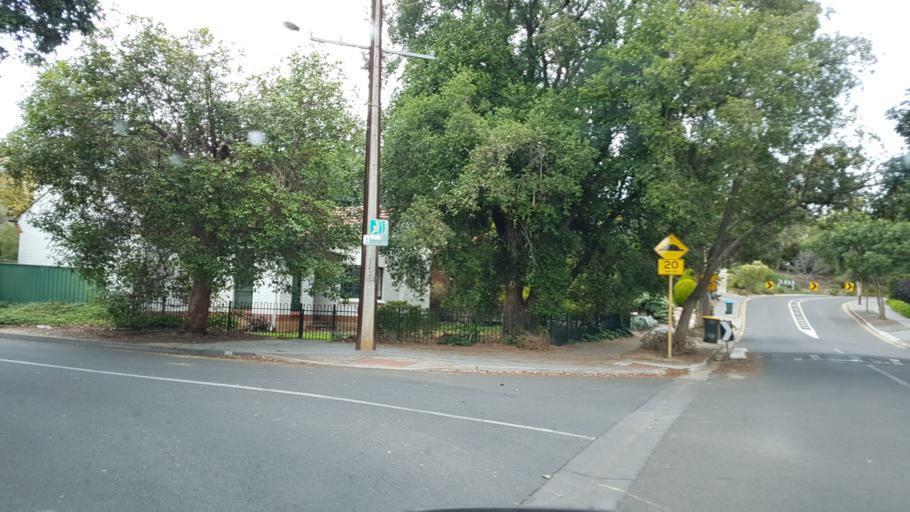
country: AU
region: South Australia
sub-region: Mitcham
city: Mitcham
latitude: -34.9799
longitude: 138.6143
